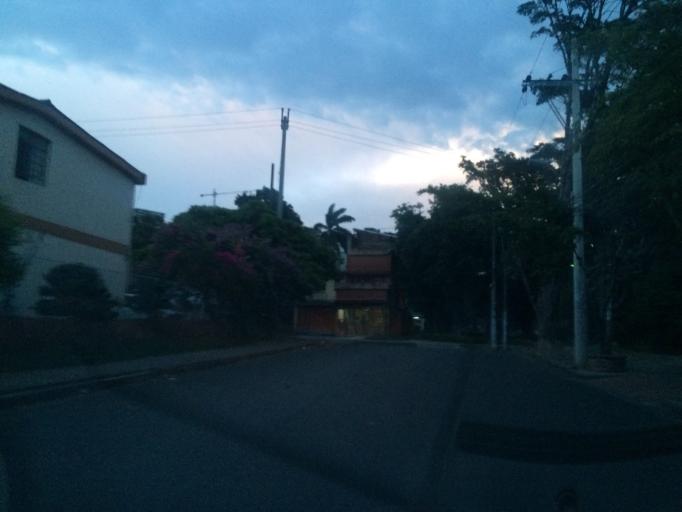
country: CO
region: Valle del Cauca
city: Cali
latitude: 3.4254
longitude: -76.5505
